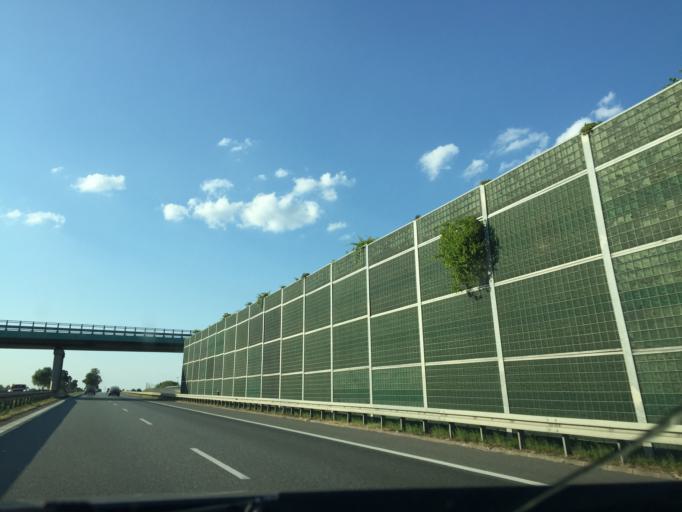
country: PL
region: Masovian Voivodeship
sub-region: Powiat bialobrzeski
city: Stara Blotnica
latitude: 51.5835
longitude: 21.0004
